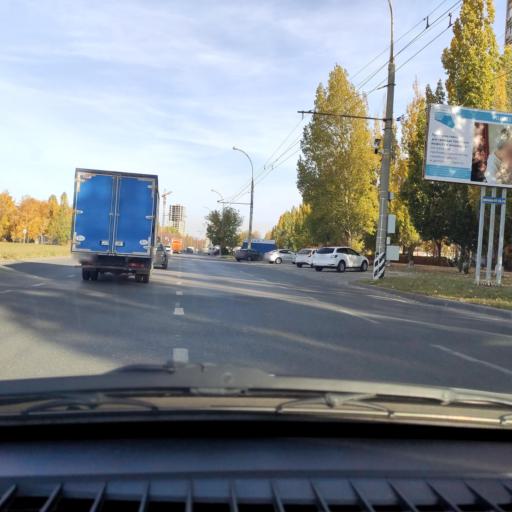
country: RU
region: Samara
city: Tol'yatti
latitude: 53.5200
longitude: 49.2956
